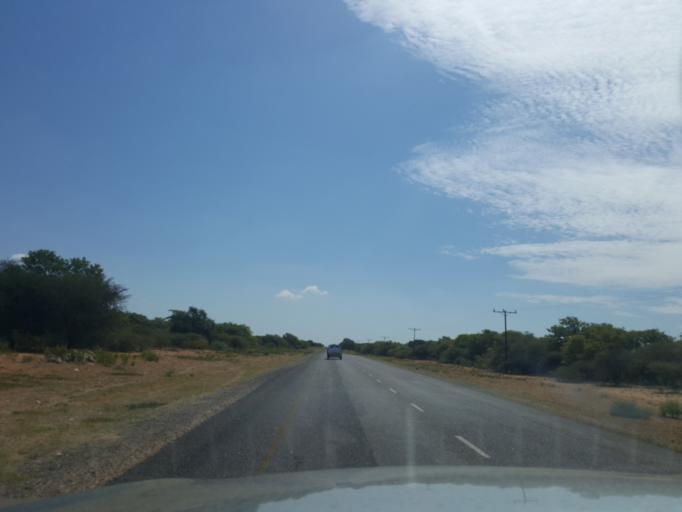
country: BW
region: Kweneng
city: Letlhakeng
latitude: -24.1253
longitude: 25.1060
